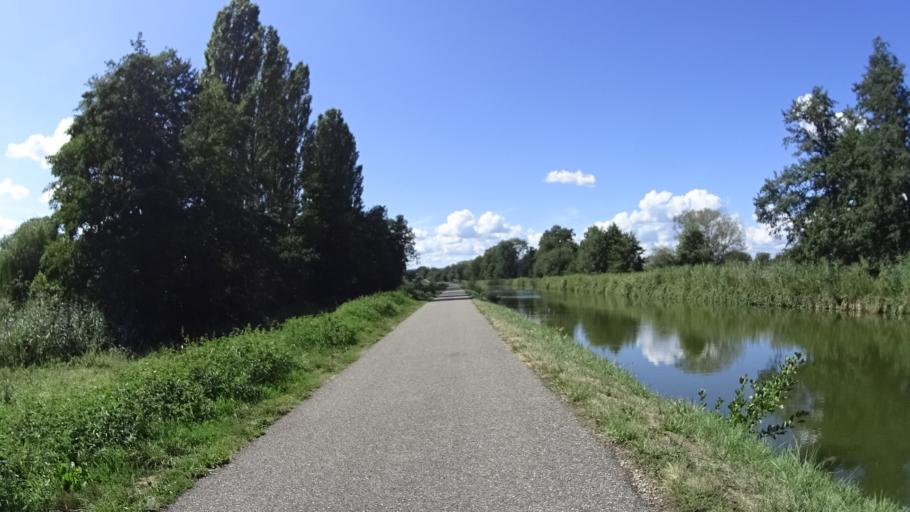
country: FR
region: Alsace
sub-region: Departement du Haut-Rhin
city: Aspach
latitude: 47.6627
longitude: 7.2039
